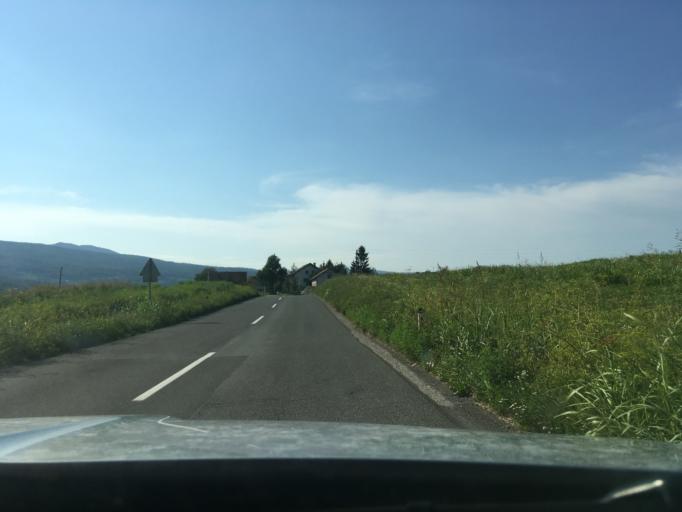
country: SI
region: Crnomelj
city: Crnomelj
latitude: 45.5176
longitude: 15.1788
